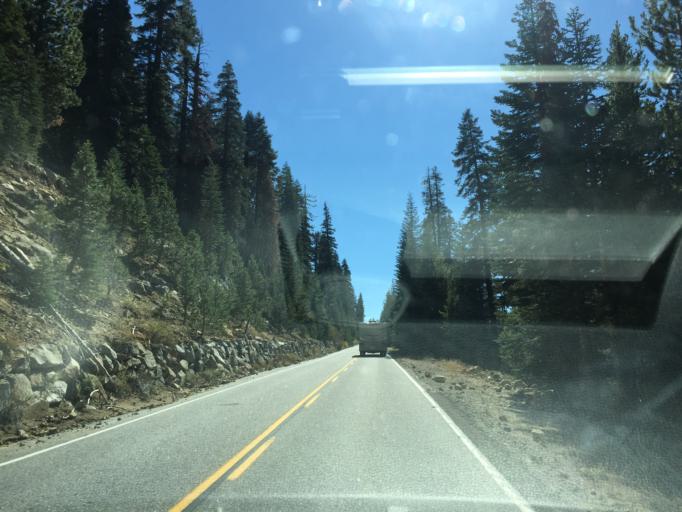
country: US
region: California
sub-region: Mariposa County
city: Yosemite Valley
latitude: 37.8426
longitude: -119.5741
